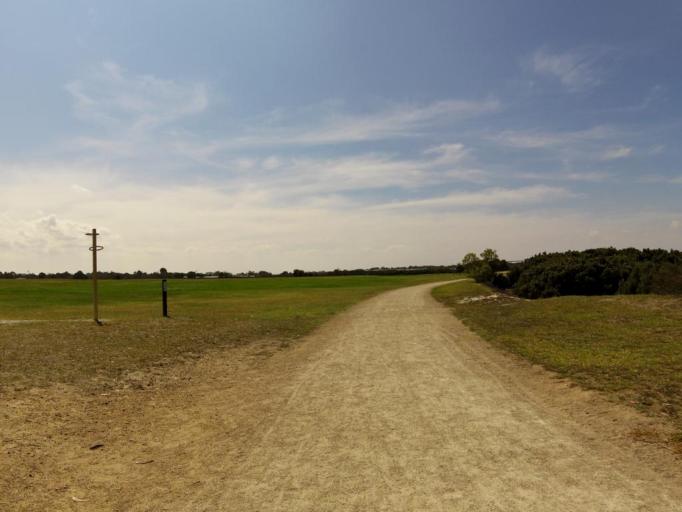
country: AU
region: Victoria
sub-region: Mornington Peninsula
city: Hastings
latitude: -38.3031
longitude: 145.1953
